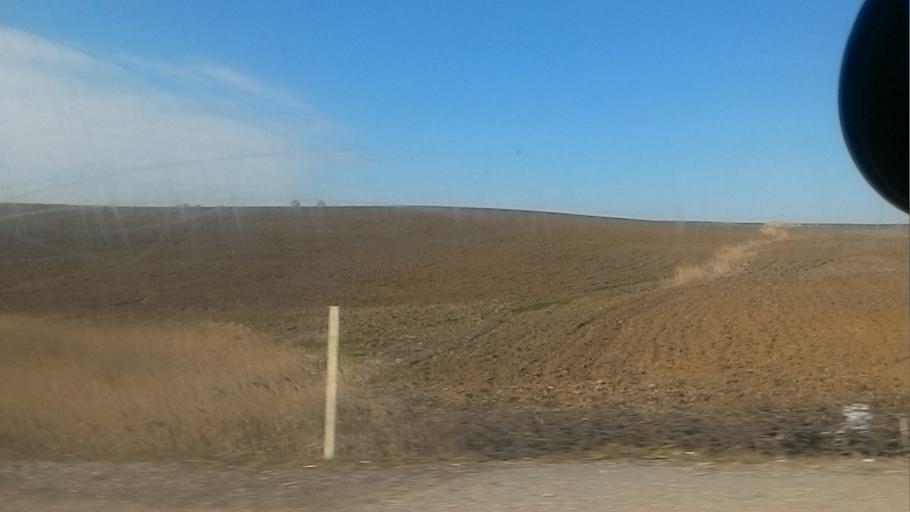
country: TR
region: Istanbul
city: Silivri
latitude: 41.0770
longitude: 28.1749
